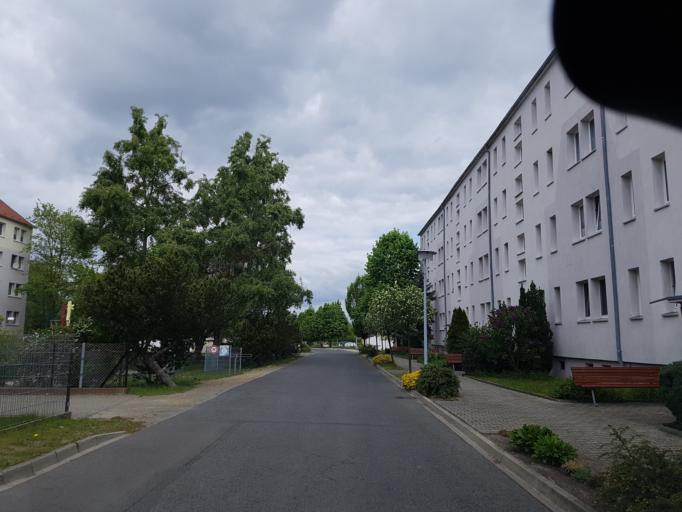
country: DE
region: Brandenburg
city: Altdobern
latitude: 51.6484
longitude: 14.0192
